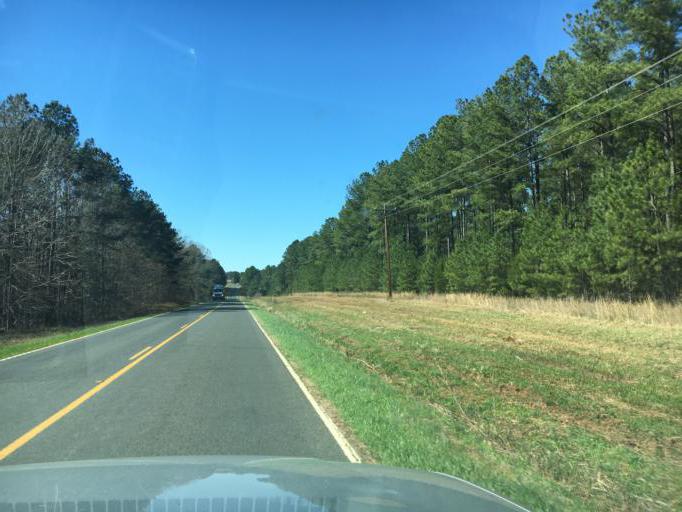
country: US
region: South Carolina
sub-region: Greenwood County
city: Ninety Six
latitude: 34.2912
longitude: -81.9649
